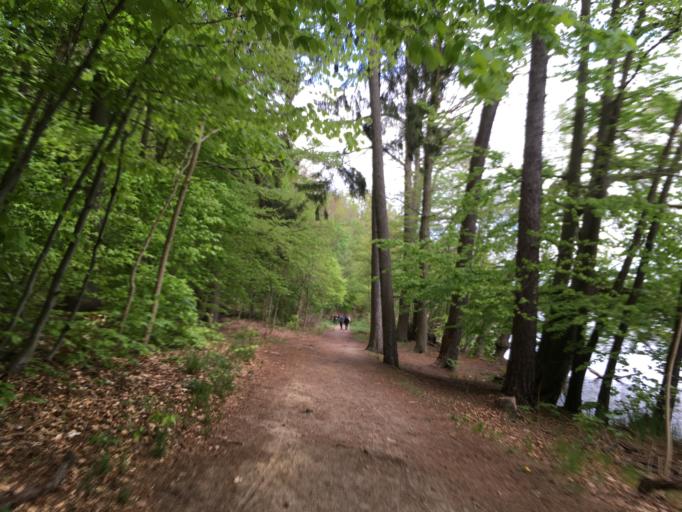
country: DE
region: Brandenburg
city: Rudnitz
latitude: 52.7609
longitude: 13.5490
